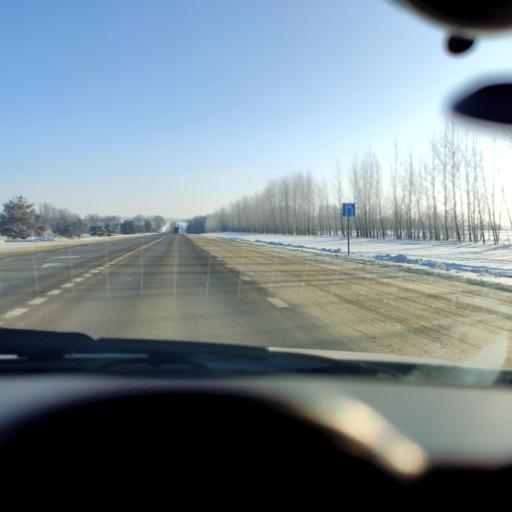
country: RU
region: Kursk
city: Tim
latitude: 51.6530
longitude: 36.9477
